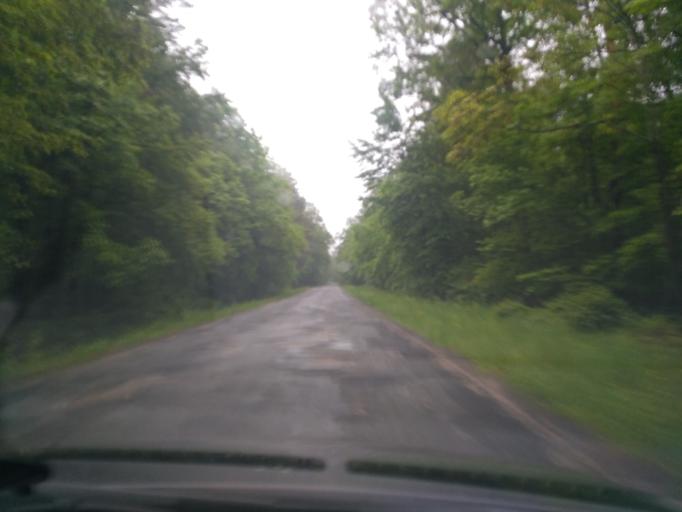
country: PL
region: Subcarpathian Voivodeship
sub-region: Powiat debicki
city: Pilzno
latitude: 49.9746
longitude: 21.3711
